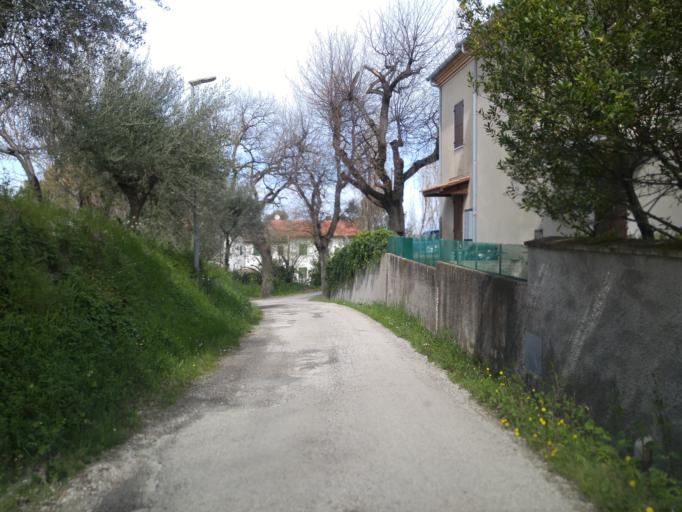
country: IT
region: The Marches
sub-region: Provincia di Pesaro e Urbino
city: Cartoceto
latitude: 43.7677
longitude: 12.8958
